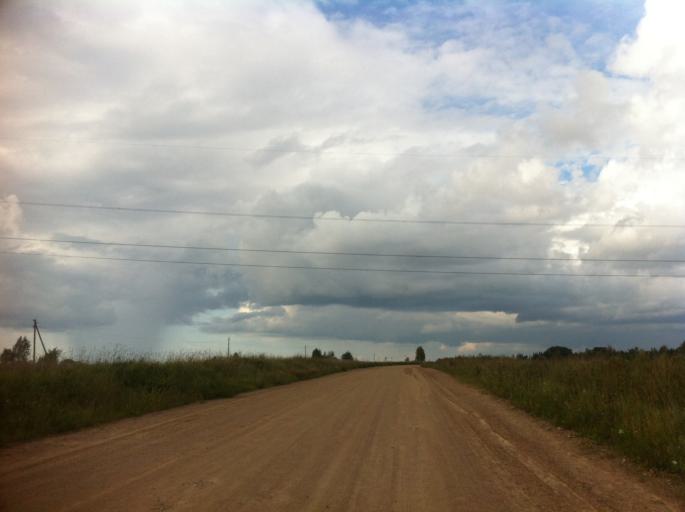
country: RU
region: Pskov
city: Izborsk
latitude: 57.8307
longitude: 27.9829
